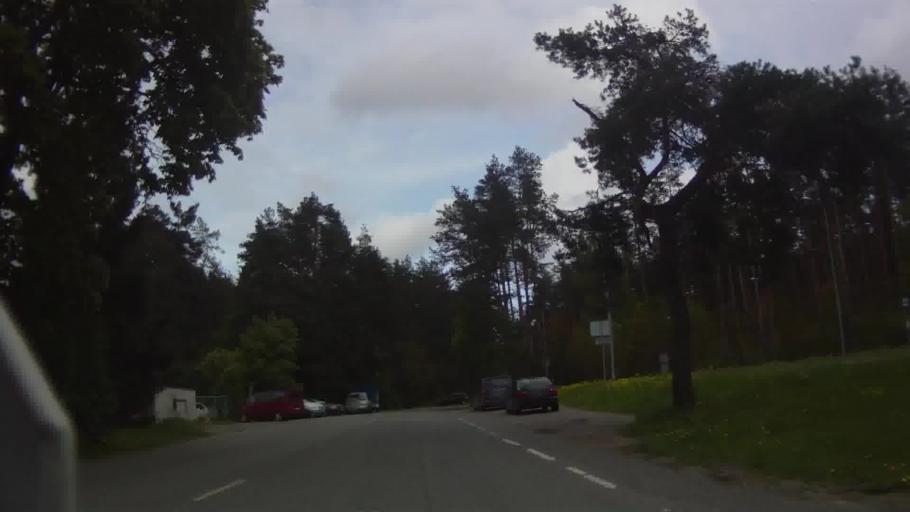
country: LV
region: Stopini
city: Ulbroka
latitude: 56.9564
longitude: 24.2559
